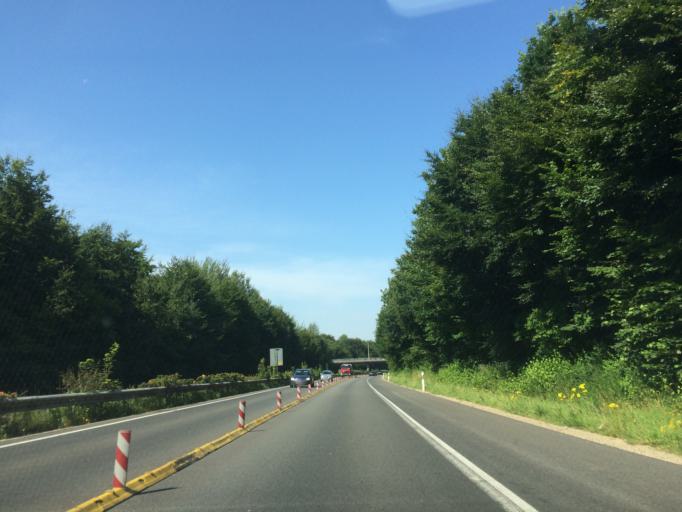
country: DE
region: Schleswig-Holstein
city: Kronshagen
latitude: 54.3520
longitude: 10.1090
